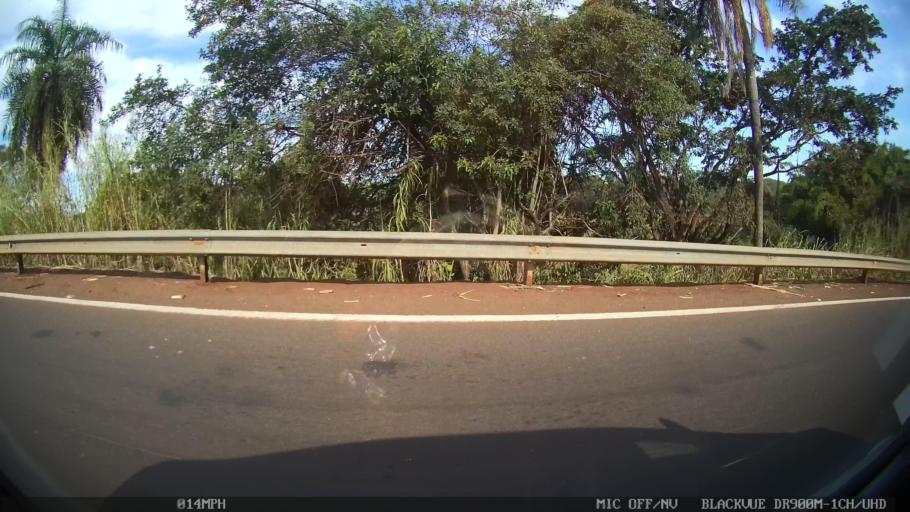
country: BR
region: Sao Paulo
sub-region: Americo Brasiliense
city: Americo Brasiliense
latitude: -21.7555
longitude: -48.0686
